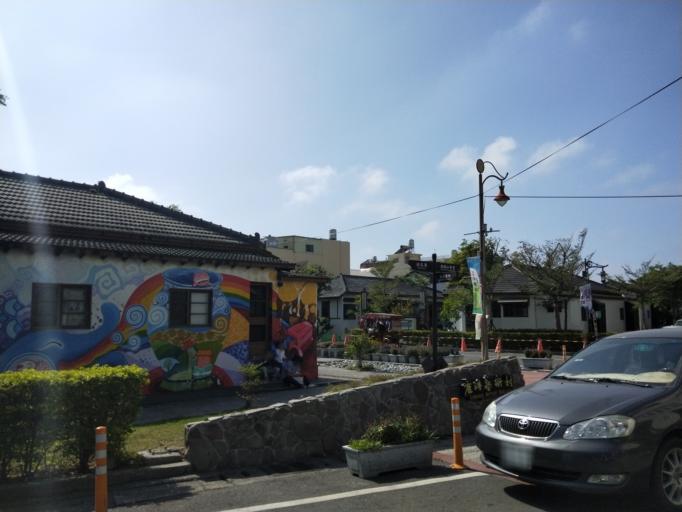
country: TW
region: Taiwan
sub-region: Changhua
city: Chang-hua
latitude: 24.0559
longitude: 120.4323
